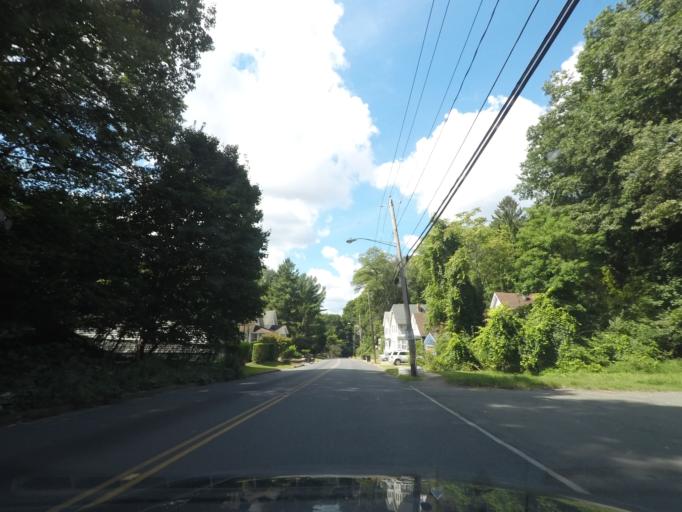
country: US
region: New York
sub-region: Rensselaer County
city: Troy
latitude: 42.7171
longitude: -73.6782
